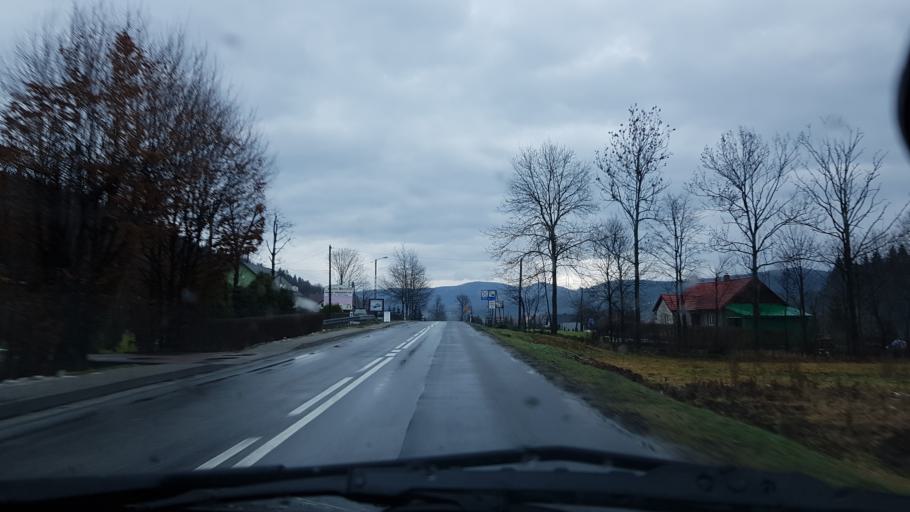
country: PL
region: Lesser Poland Voivodeship
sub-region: Powiat suski
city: Kukow
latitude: 49.7369
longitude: 19.4698
